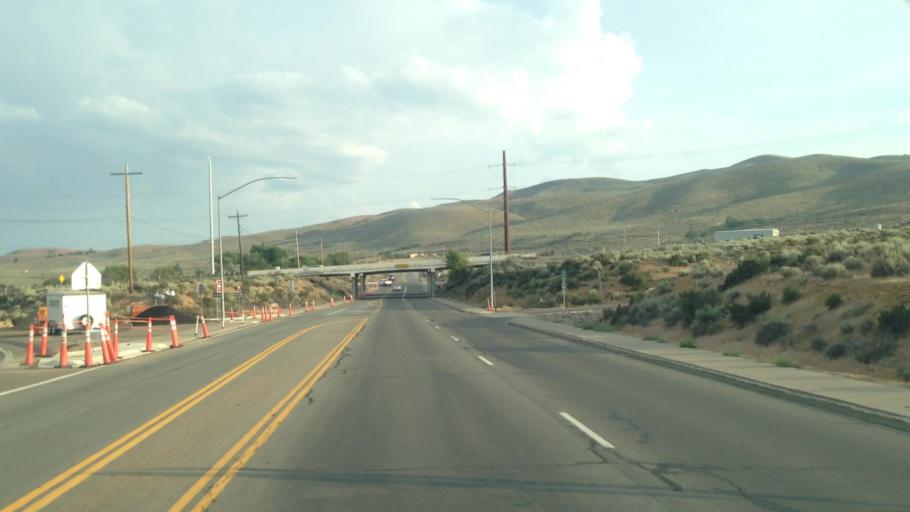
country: US
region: Nevada
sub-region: Washoe County
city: Lemmon Valley
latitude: 39.6207
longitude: -119.8822
